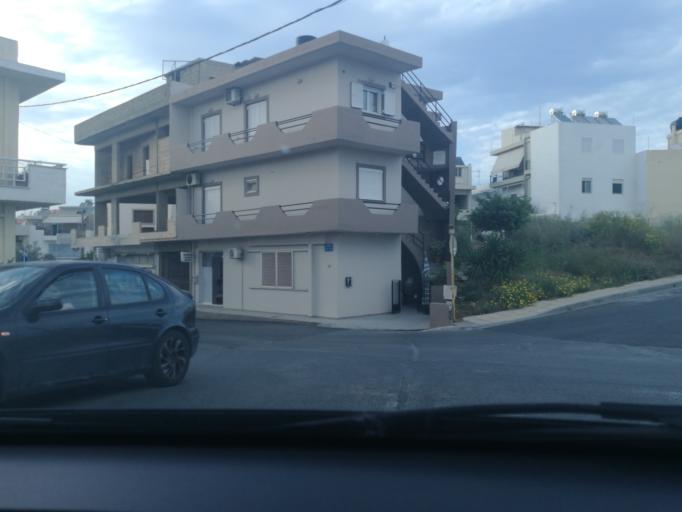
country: GR
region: Crete
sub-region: Nomos Irakleiou
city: Irakleion
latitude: 35.3151
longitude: 25.1395
